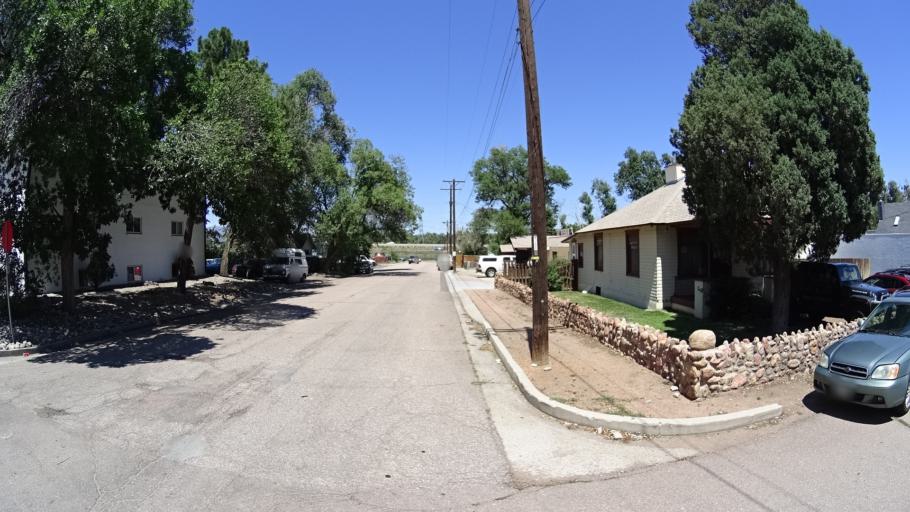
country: US
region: Colorado
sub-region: El Paso County
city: Colorado Springs
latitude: 38.8128
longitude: -104.8192
